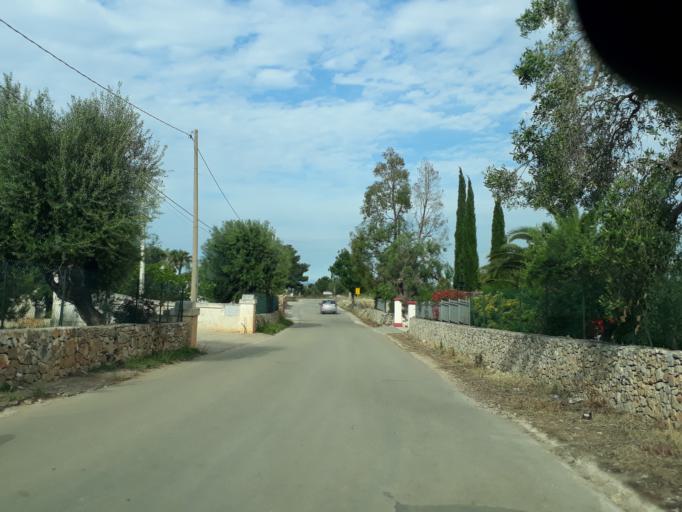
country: IT
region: Apulia
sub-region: Provincia di Brindisi
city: Pezze di Greco
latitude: 40.8042
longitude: 17.4058
